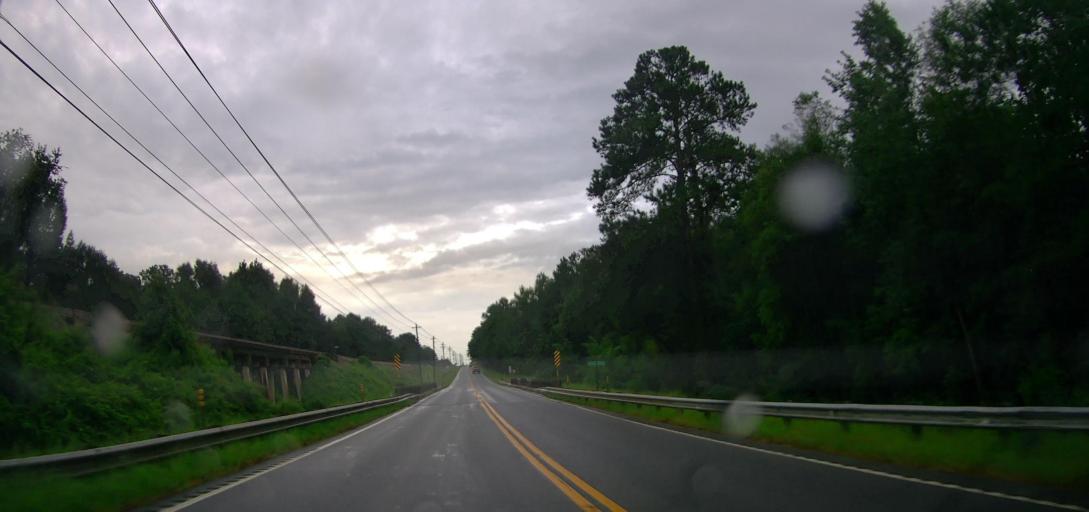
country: US
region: Georgia
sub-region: Ware County
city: Deenwood
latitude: 31.2580
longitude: -82.3786
